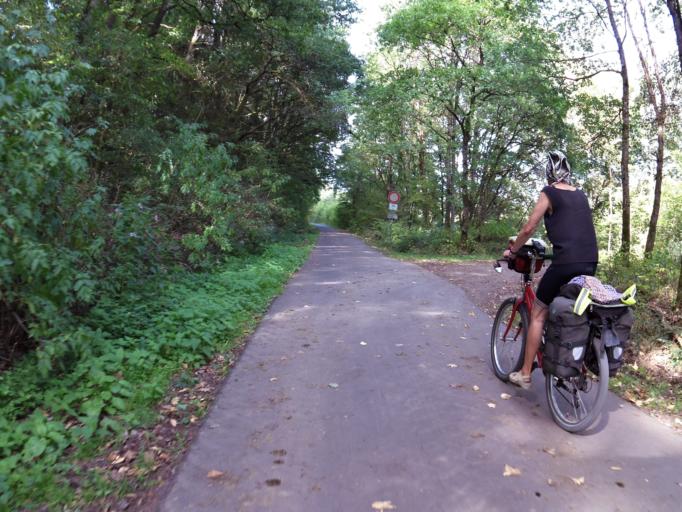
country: DE
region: Rheinland-Pfalz
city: Pronsfeld
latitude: 50.1510
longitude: 6.3364
